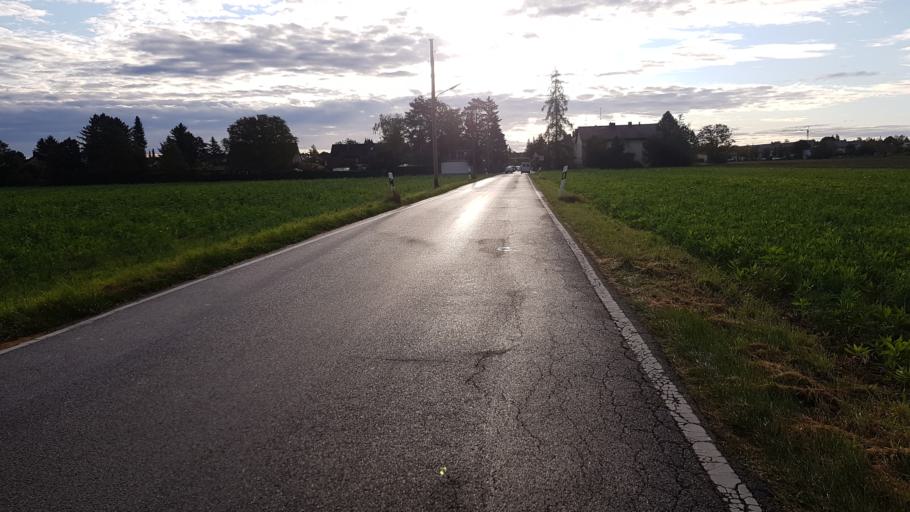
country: DE
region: Bavaria
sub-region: Upper Bavaria
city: Neubiberg
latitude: 48.0821
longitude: 11.6537
